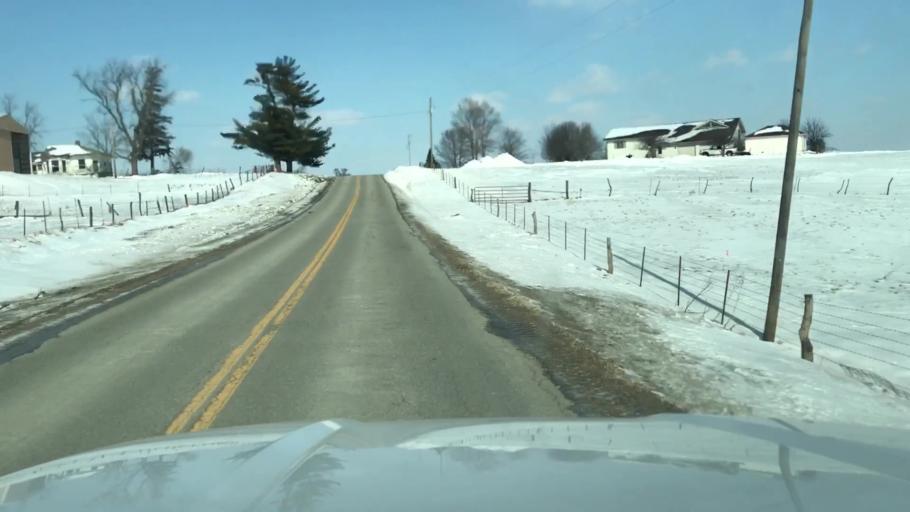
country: US
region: Missouri
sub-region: Nodaway County
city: Maryville
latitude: 40.3813
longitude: -94.7215
